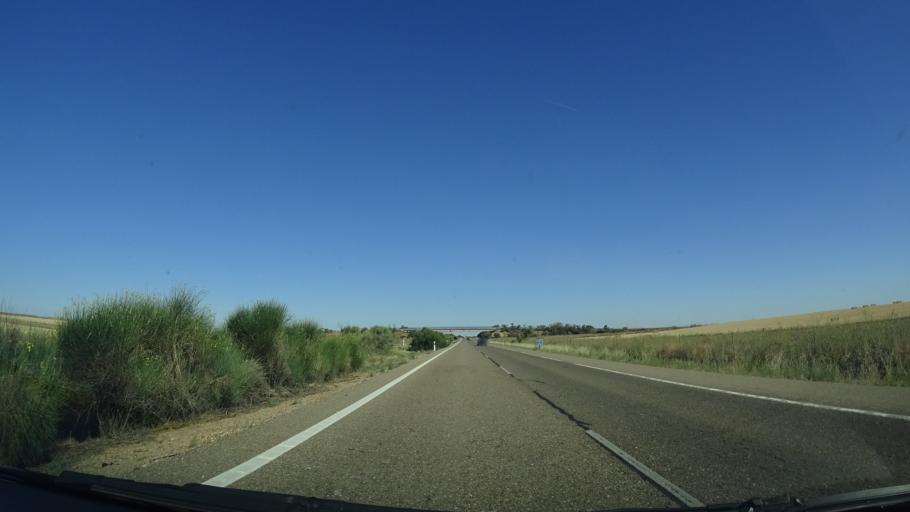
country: ES
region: Castille and Leon
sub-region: Provincia de Valladolid
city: Villanueva de los Caballeros
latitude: 41.7467
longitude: -5.2770
